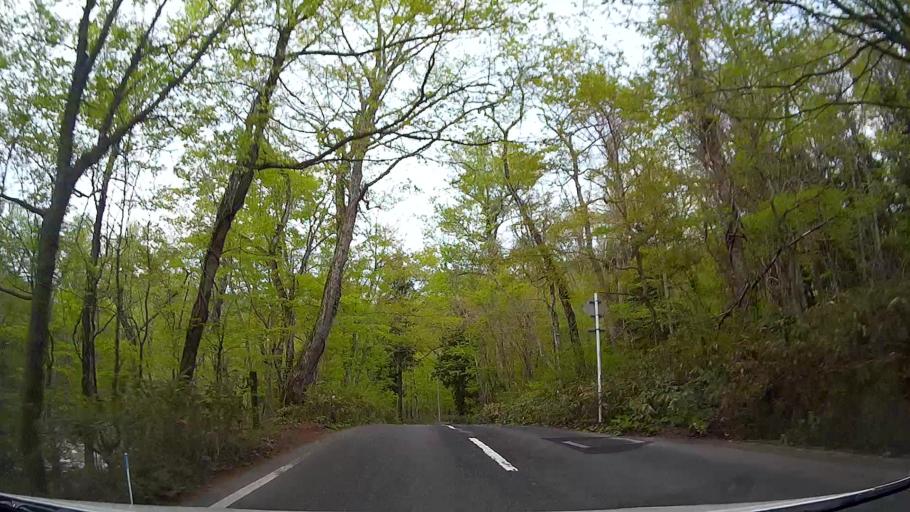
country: JP
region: Aomori
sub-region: Aomori Shi
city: Furudate
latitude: 40.5670
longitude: 140.9757
